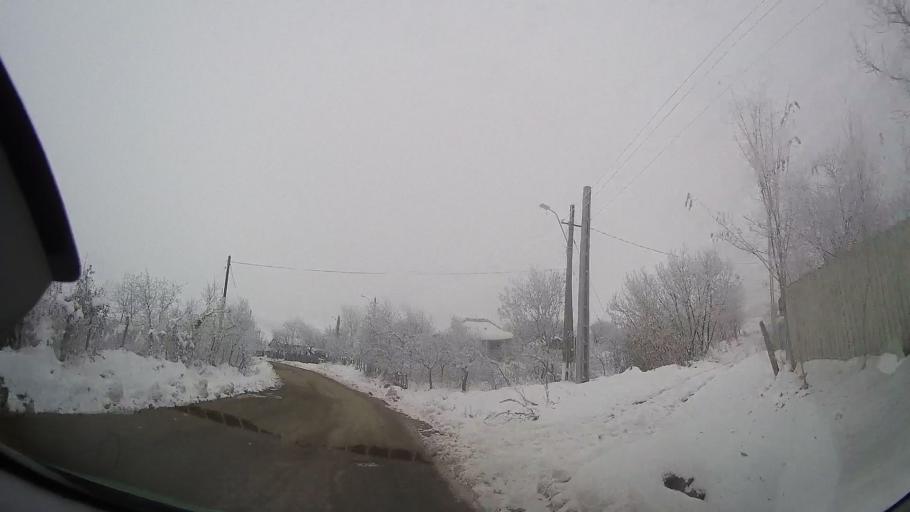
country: RO
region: Iasi
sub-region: Comuna Tansa
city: Tansa
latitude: 46.9137
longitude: 27.2255
